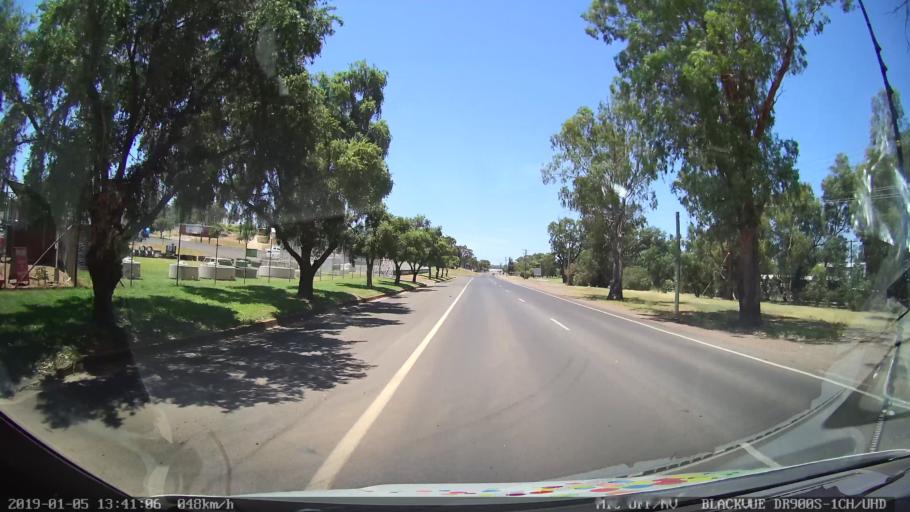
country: AU
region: New South Wales
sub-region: Gunnedah
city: Gunnedah
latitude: -30.9796
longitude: 150.2364
